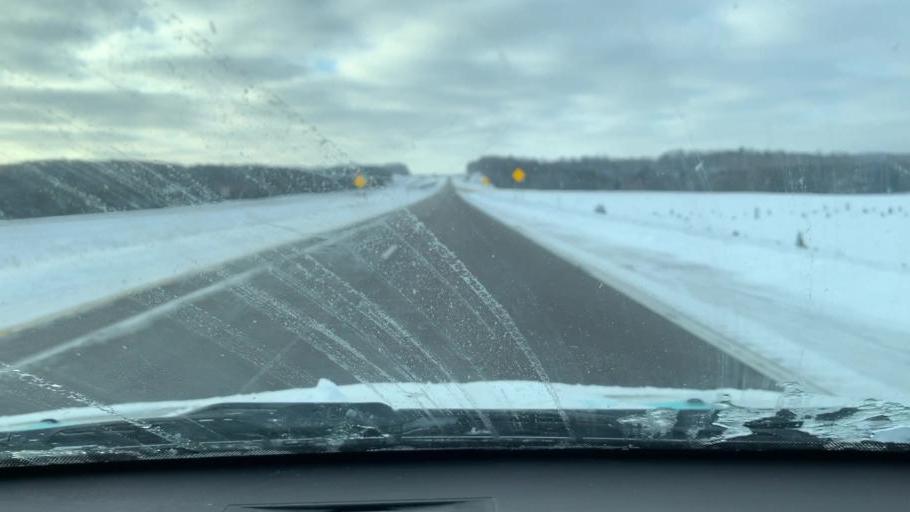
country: US
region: Michigan
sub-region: Wexford County
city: Manton
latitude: 44.4065
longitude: -85.3814
